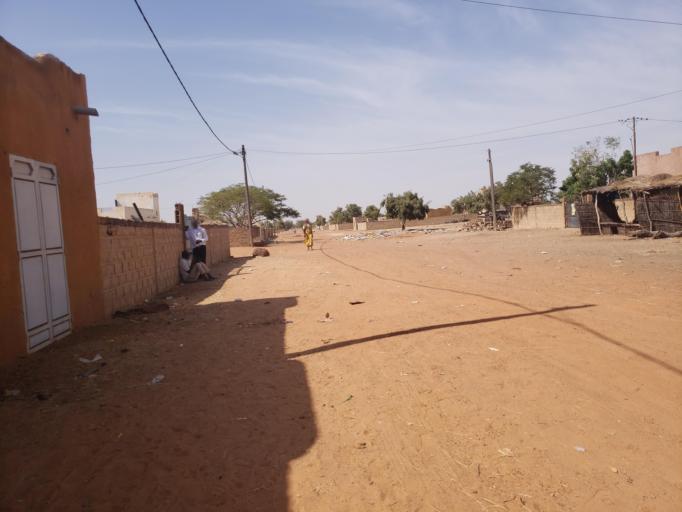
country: SN
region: Matam
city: Ranerou
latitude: 15.2993
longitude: -13.9631
